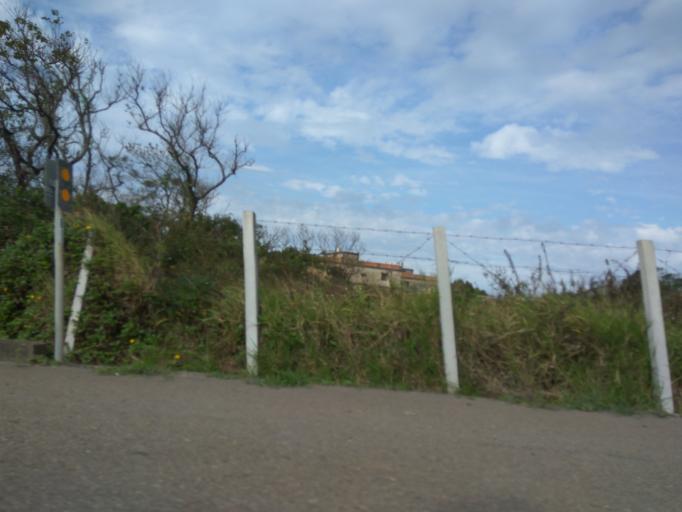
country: TW
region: Taiwan
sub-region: Hsinchu
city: Zhubei
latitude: 24.9669
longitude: 121.0172
